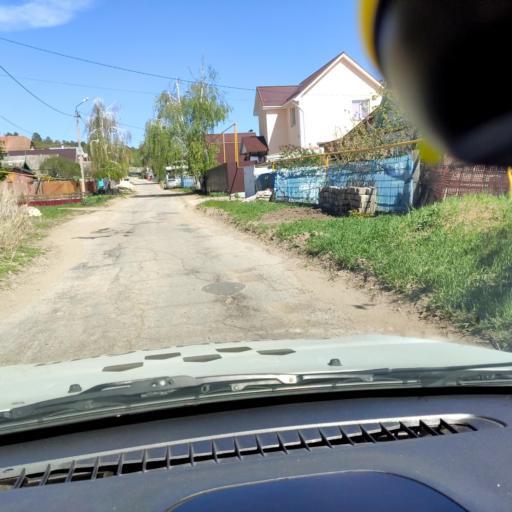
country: RU
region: Samara
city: Zhigulevsk
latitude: 53.4690
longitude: 49.6421
